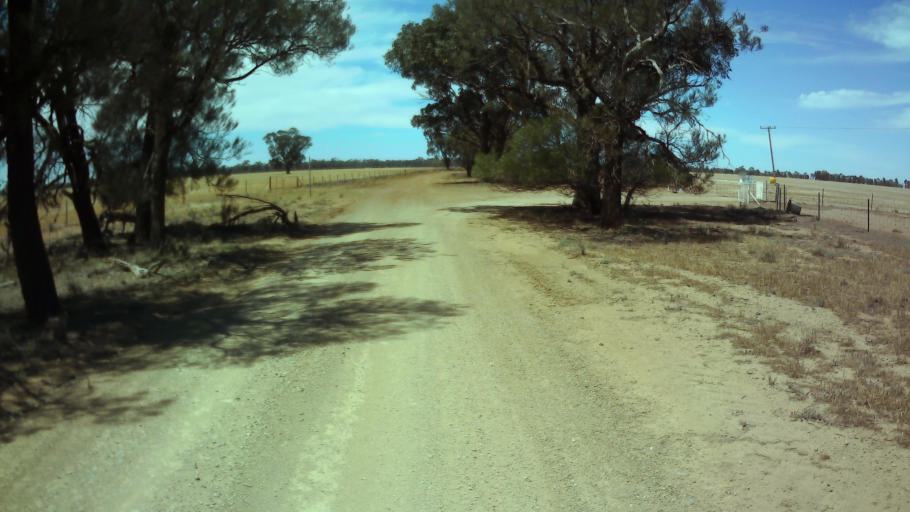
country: AU
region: New South Wales
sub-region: Weddin
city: Grenfell
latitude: -33.8917
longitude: 147.8029
